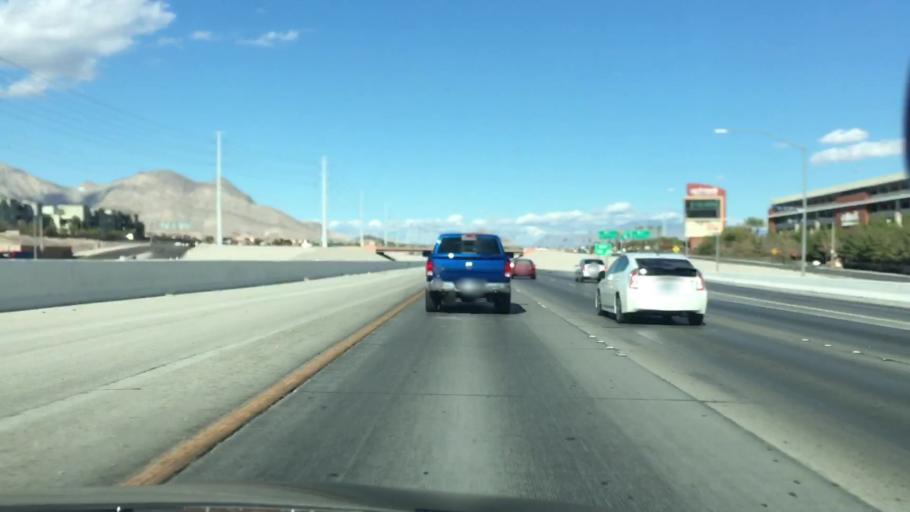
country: US
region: Nevada
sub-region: Clark County
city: Summerlin South
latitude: 36.1546
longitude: -115.3370
